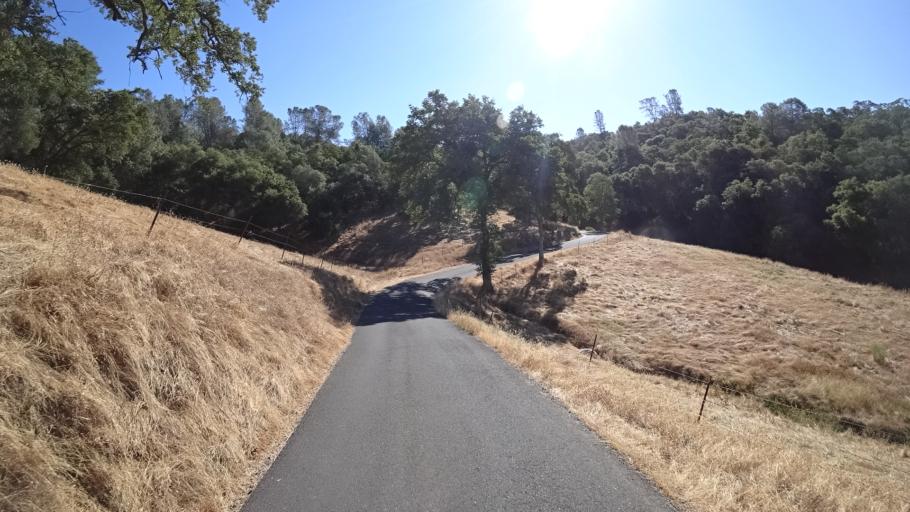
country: US
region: California
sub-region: Calaveras County
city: San Andreas
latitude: 38.2272
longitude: -120.6731
